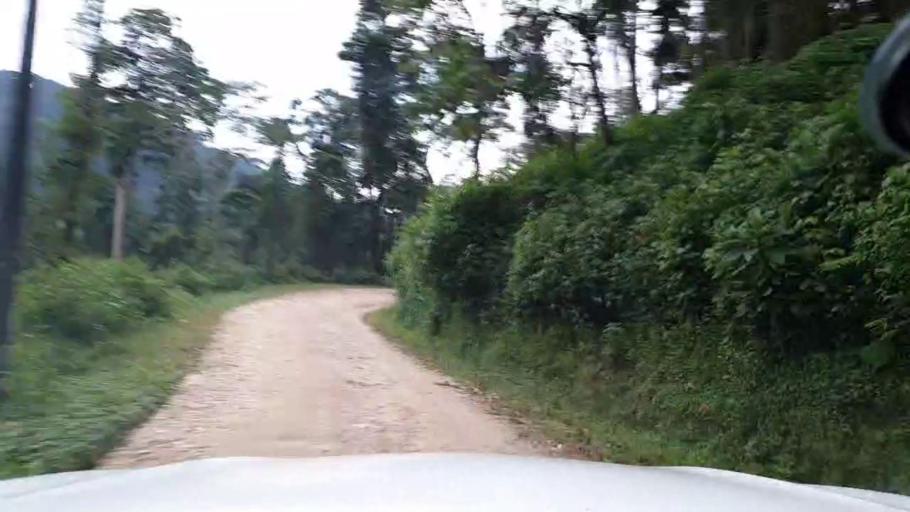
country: RW
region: Western Province
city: Cyangugu
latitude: -2.5573
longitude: 29.2314
